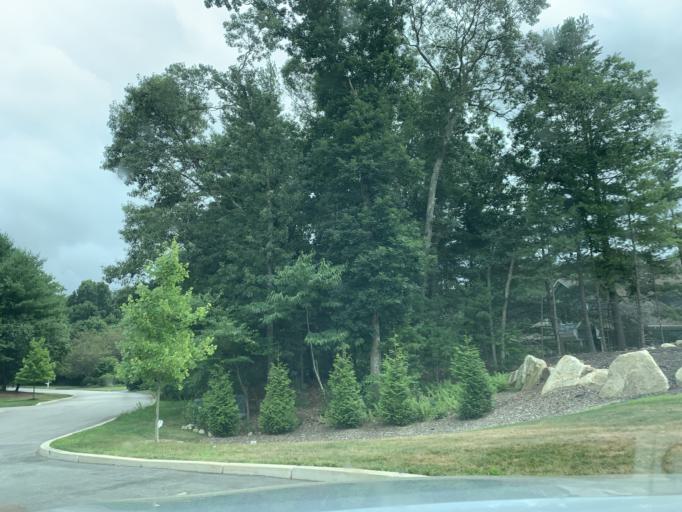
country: US
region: Rhode Island
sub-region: Kent County
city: West Warwick
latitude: 41.6547
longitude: -71.5273
